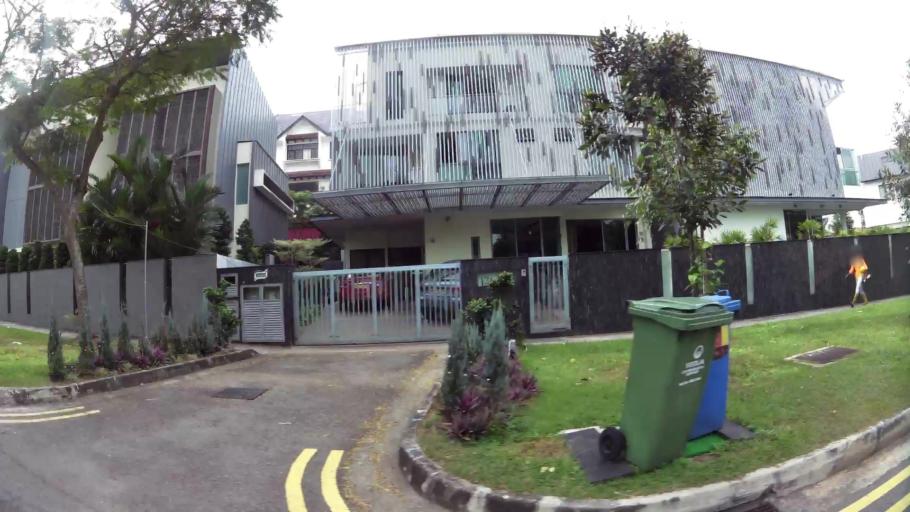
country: SG
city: Singapore
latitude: 1.3277
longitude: 103.7937
